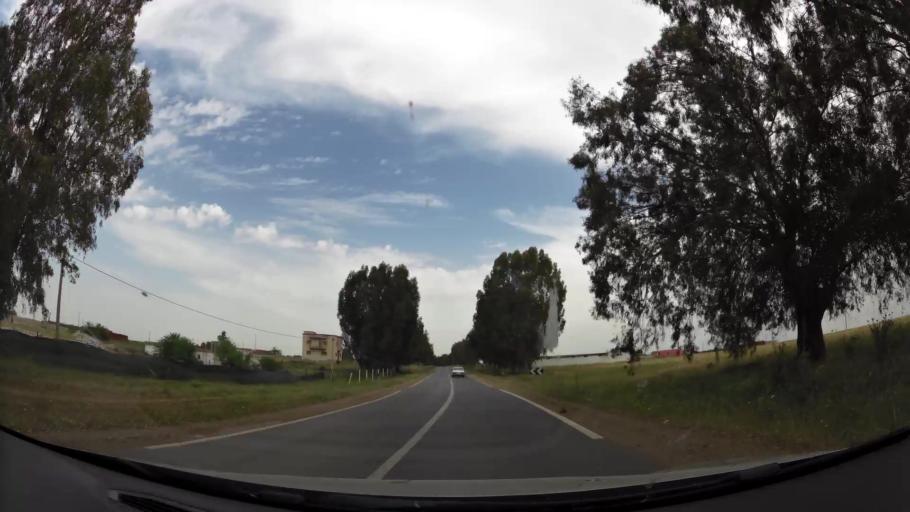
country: MA
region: Rabat-Sale-Zemmour-Zaer
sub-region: Khemisset
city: Tiflet
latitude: 33.8736
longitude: -6.2796
